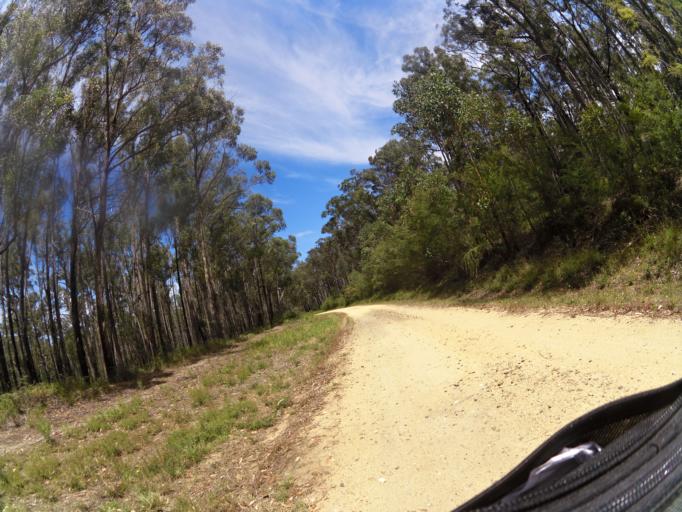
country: AU
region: Victoria
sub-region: East Gippsland
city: Lakes Entrance
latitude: -37.7313
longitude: 148.0827
